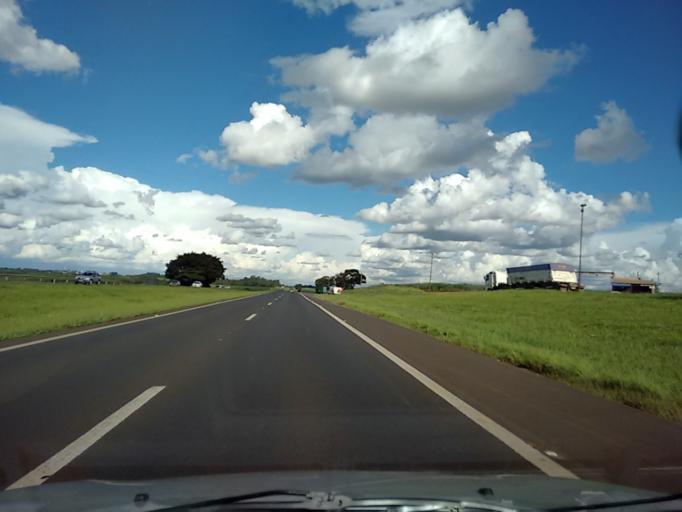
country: BR
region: Sao Paulo
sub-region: Ibate
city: Ibate
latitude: -21.9657
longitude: -47.9670
